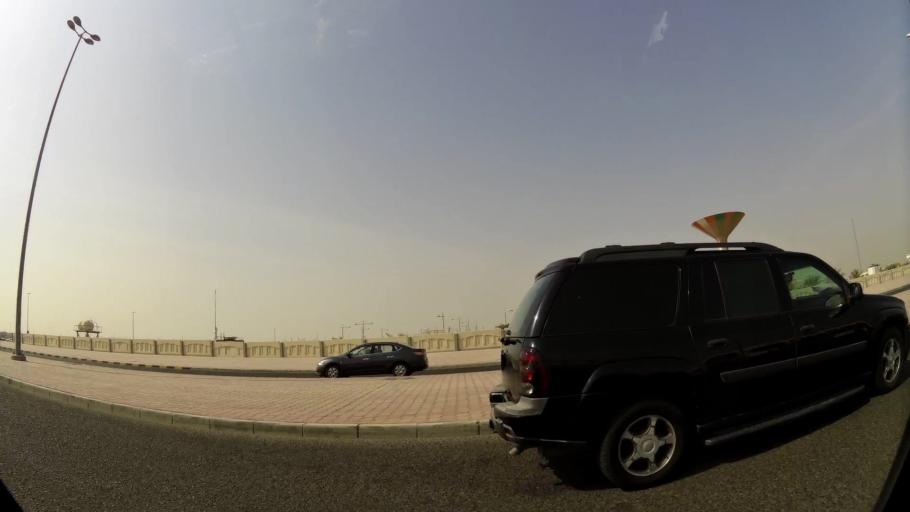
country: KW
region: Al Asimah
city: Ar Rabiyah
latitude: 29.2760
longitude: 47.9154
